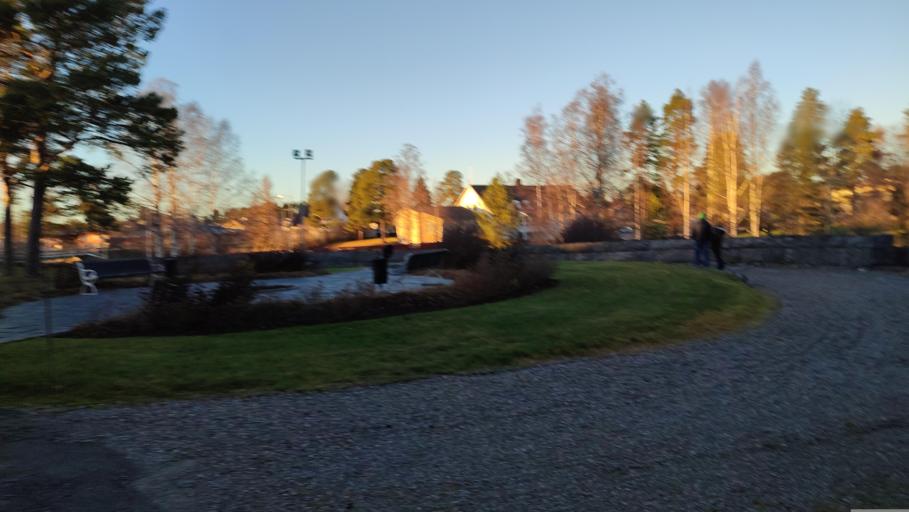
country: SE
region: Vaesterbotten
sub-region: Skelleftea Kommun
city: Burea
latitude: 64.6183
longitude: 21.2036
